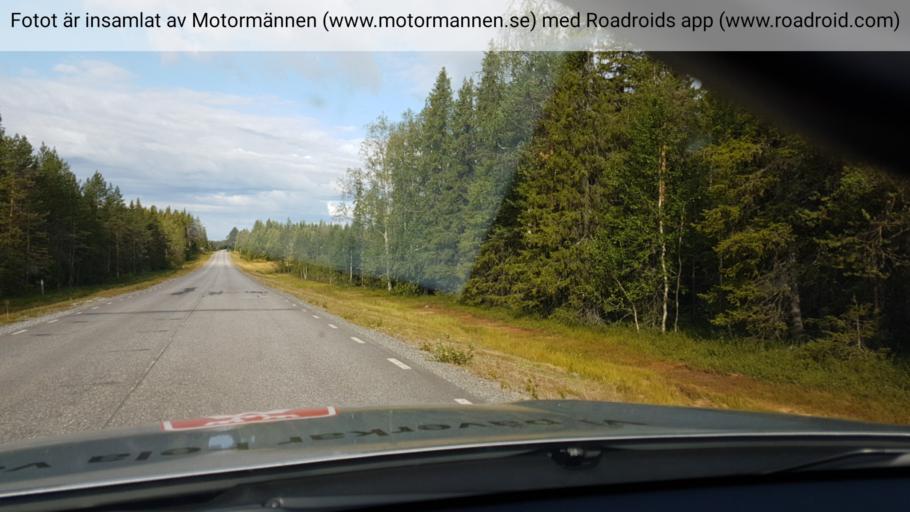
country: SE
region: Vaesterbotten
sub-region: Skelleftea Kommun
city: Storvik
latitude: 65.3366
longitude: 20.5679
